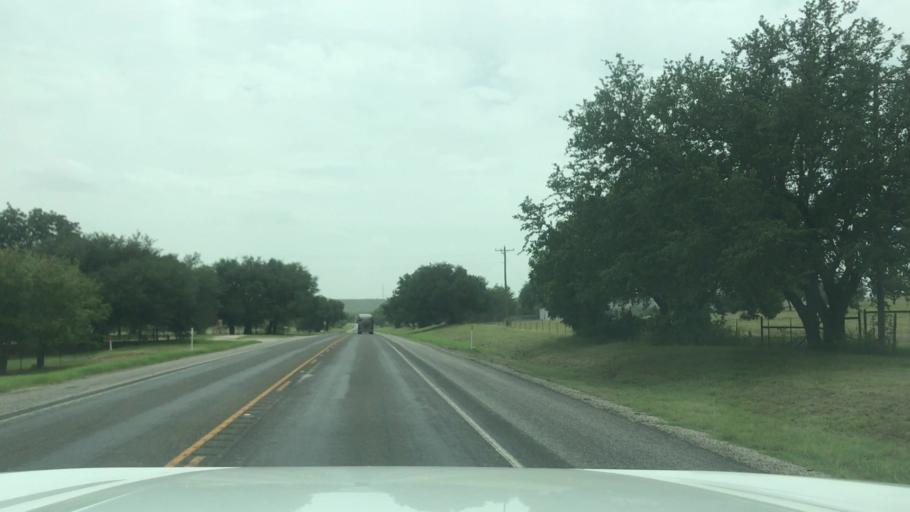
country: US
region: Texas
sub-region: Bosque County
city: Meridian
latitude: 31.8926
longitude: -97.6470
